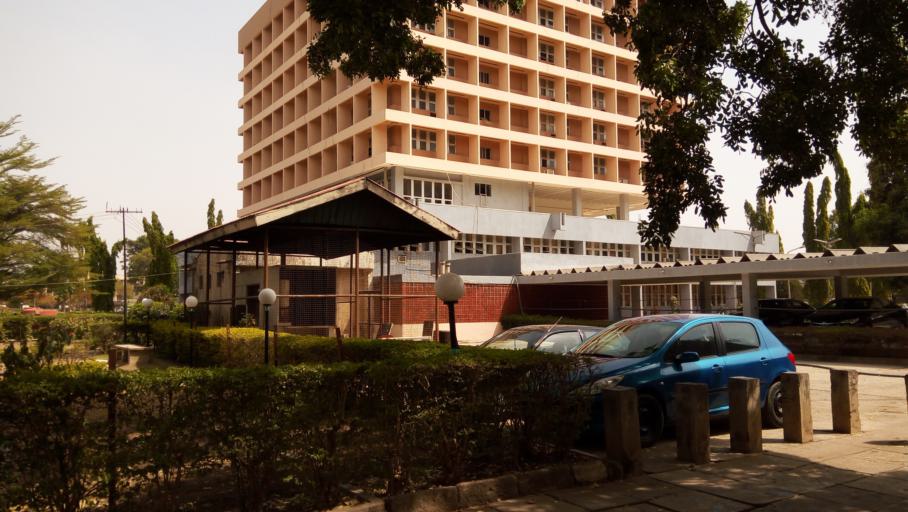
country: NG
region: Kaduna
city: Zaria
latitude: 11.1499
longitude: 7.6547
